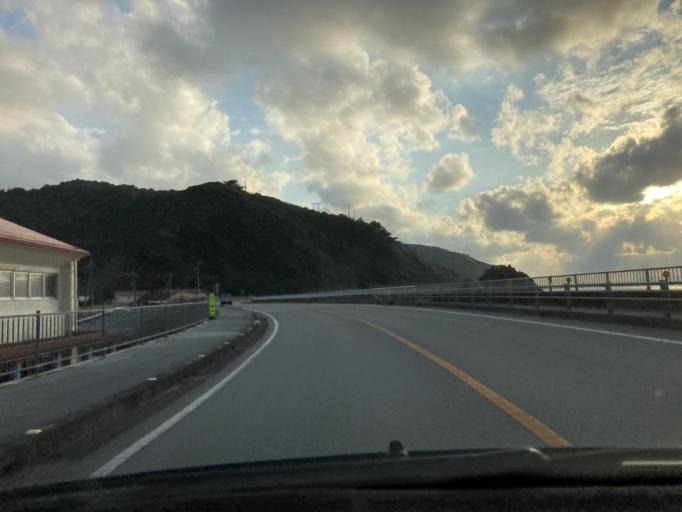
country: JP
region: Okinawa
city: Nago
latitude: 26.7856
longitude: 128.2195
